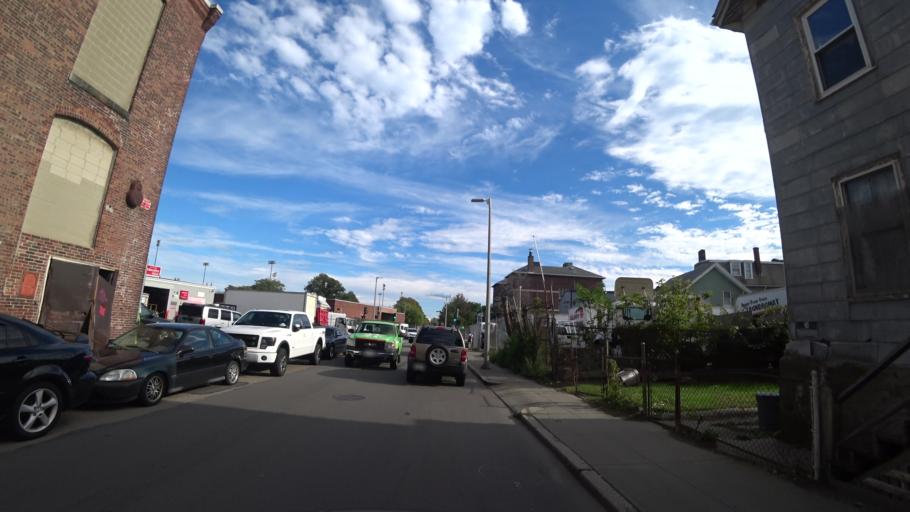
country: US
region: Massachusetts
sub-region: Suffolk County
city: South Boston
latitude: 42.3270
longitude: -71.0720
